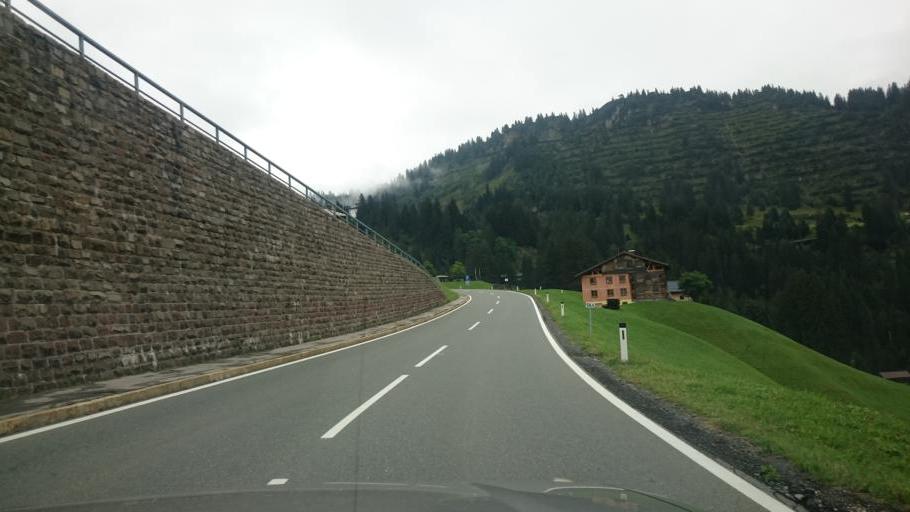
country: AT
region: Vorarlberg
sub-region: Politischer Bezirk Bregenz
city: Schroecken
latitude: 47.2611
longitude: 10.0928
